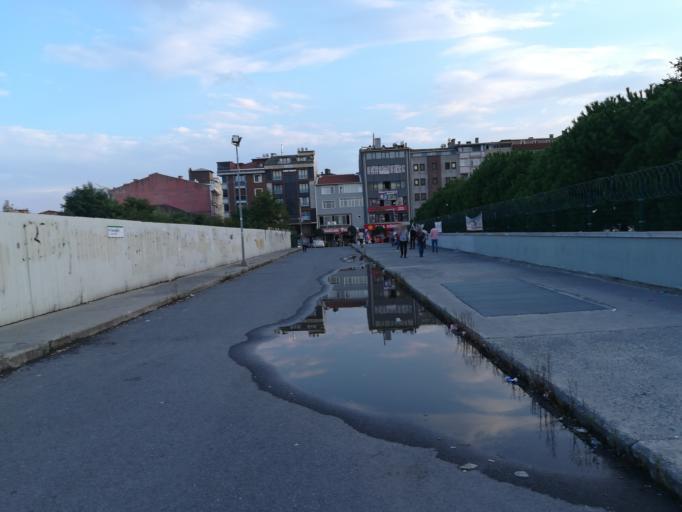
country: TR
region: Istanbul
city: Sisli
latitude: 41.1003
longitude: 28.9944
